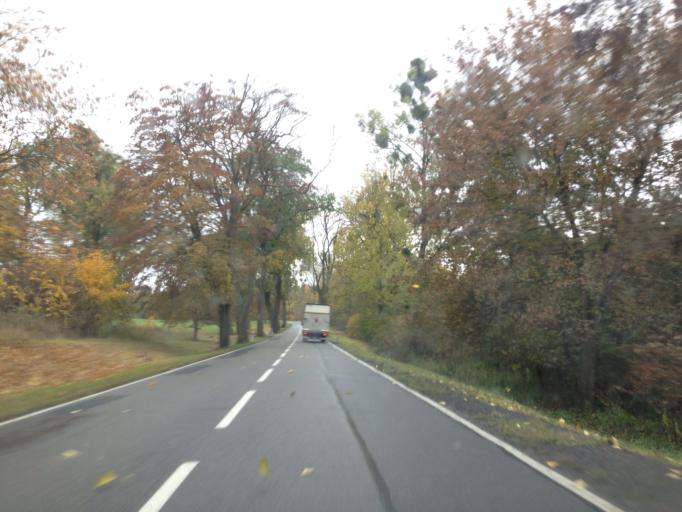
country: PL
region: Pomeranian Voivodeship
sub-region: Powiat kwidzynski
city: Ryjewo
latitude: 53.8524
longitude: 18.9993
